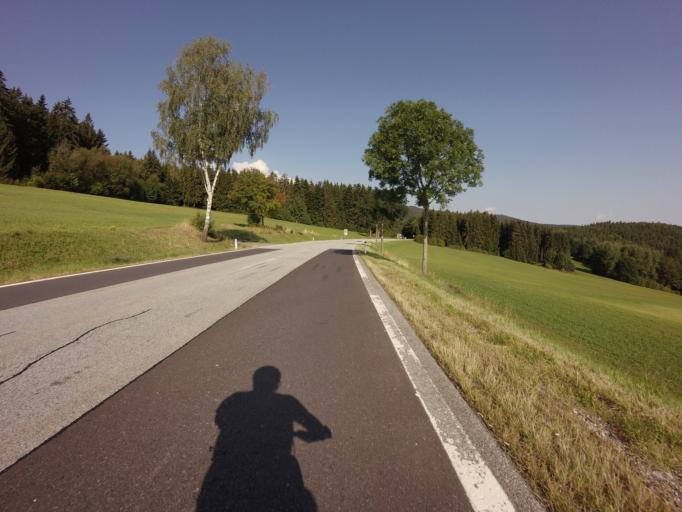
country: AT
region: Upper Austria
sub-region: Politischer Bezirk Urfahr-Umgebung
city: Bad Leonfelden
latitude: 48.5596
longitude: 14.3198
